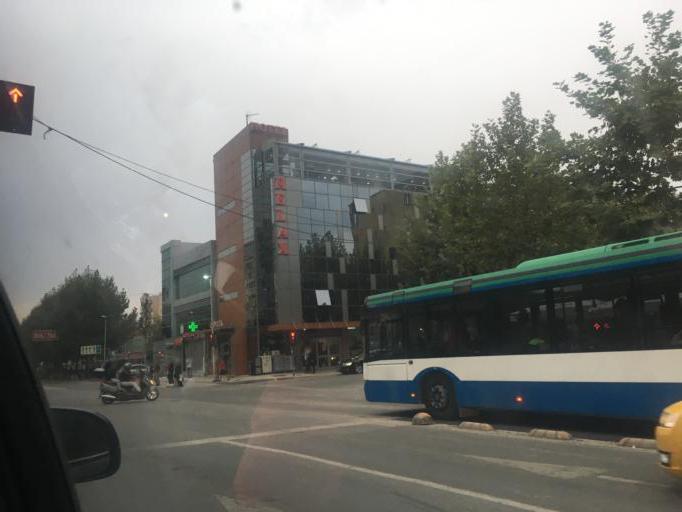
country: AL
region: Tirane
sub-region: Rrethi i Tiranes
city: Paskuqan
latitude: 41.3370
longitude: 19.7930
